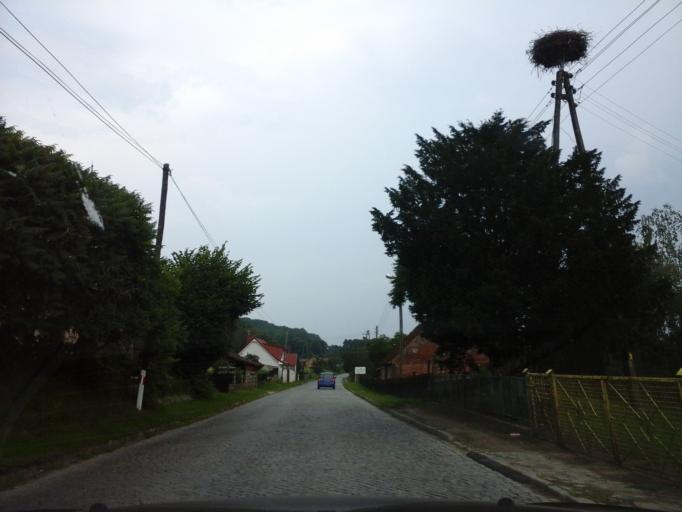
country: PL
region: Lubusz
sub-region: Powiat strzelecko-drezdenecki
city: Drezdenko
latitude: 52.8547
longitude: 15.8076
